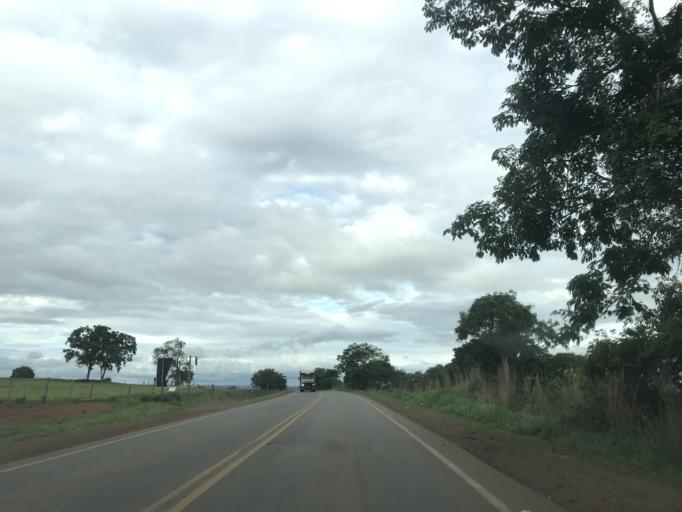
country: BR
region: Goias
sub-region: Vianopolis
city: Vianopolis
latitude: -16.7094
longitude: -48.3980
